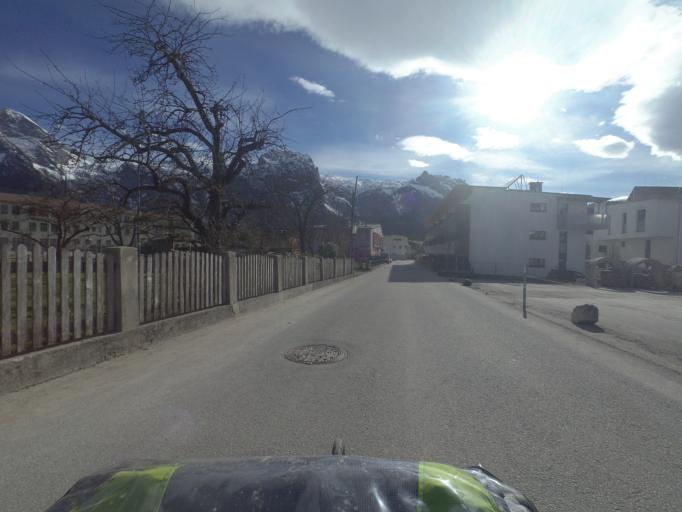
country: AT
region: Salzburg
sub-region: Politischer Bezirk Hallein
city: Abtenau
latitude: 47.5669
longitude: 13.3461
